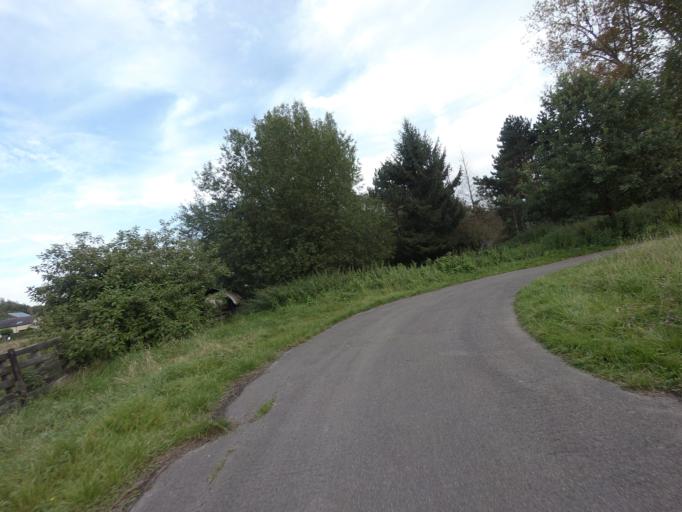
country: BE
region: Flanders
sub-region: Provincie Vlaams-Brabant
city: Boortmeerbeek
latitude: 50.9770
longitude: 4.5752
